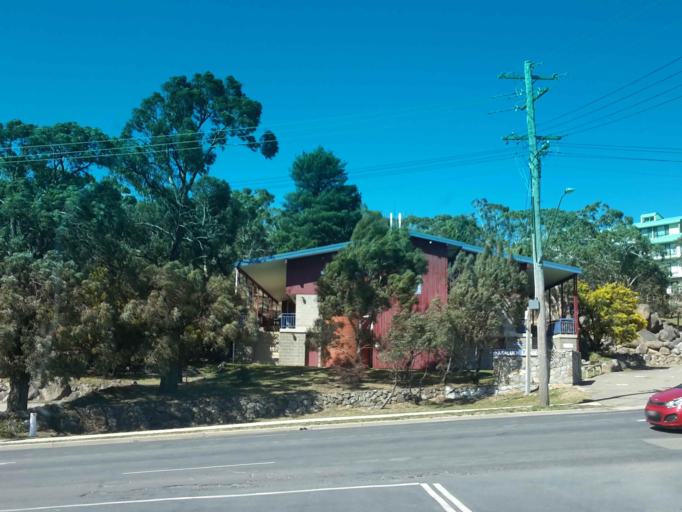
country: AU
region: New South Wales
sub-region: Snowy River
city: Jindabyne
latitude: -36.4165
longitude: 148.6111
